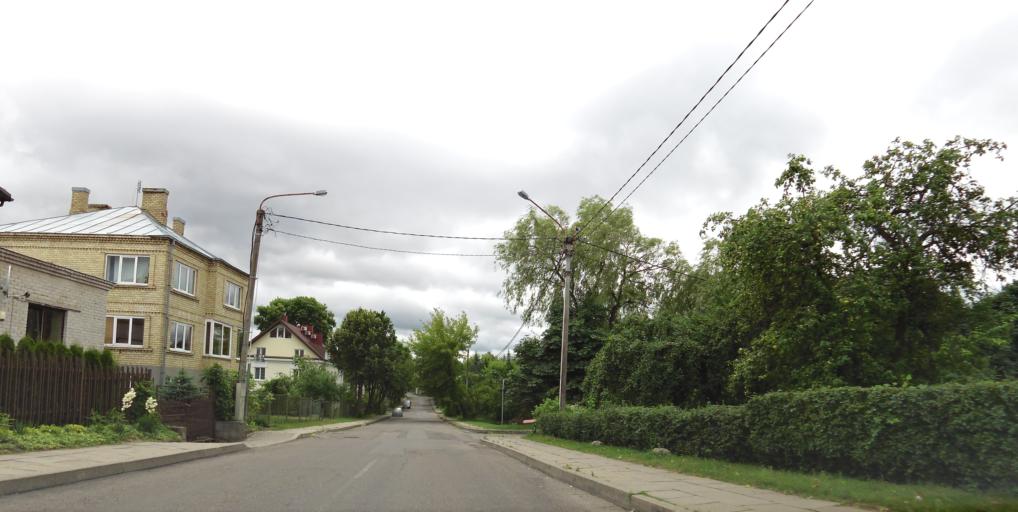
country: LT
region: Vilnius County
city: Seskine
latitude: 54.6963
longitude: 25.2458
